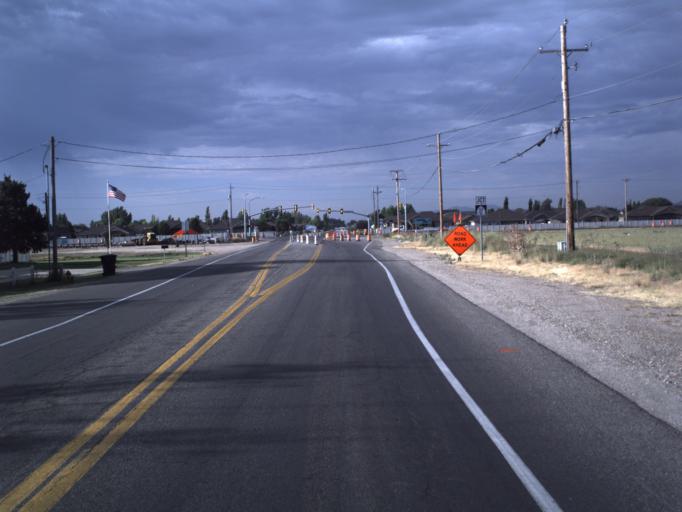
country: US
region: Utah
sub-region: Weber County
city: Hooper
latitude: 41.1926
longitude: -112.0931
